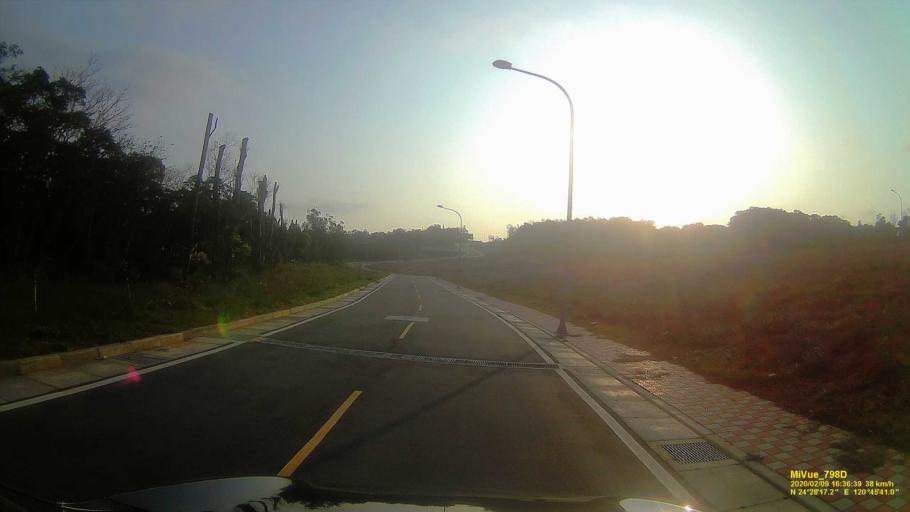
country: TW
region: Taiwan
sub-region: Miaoli
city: Miaoli
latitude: 24.4712
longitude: 120.7611
